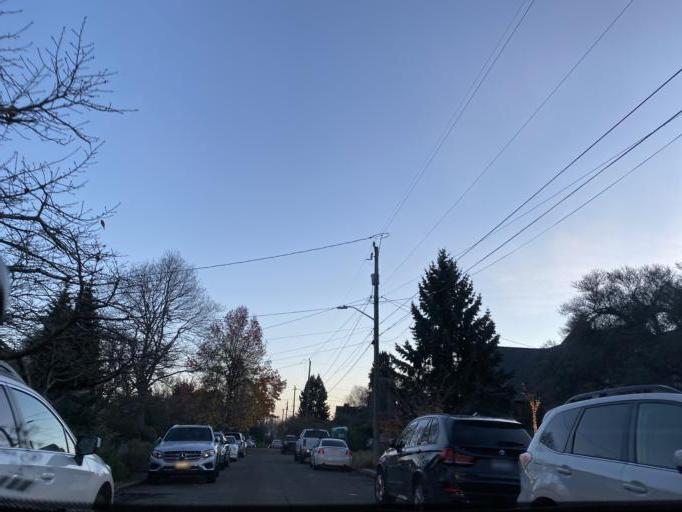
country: US
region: Washington
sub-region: King County
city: Seattle
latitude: 47.6477
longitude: -122.3915
